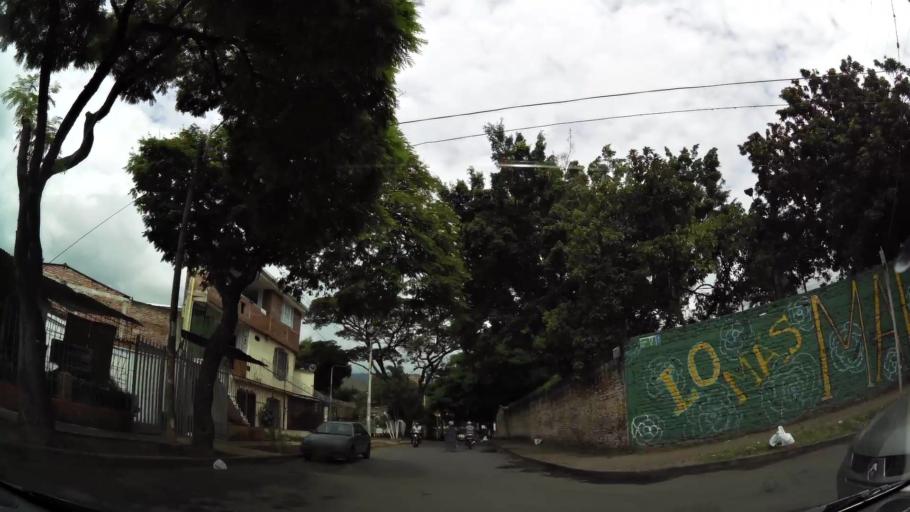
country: CO
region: Valle del Cauca
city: Cali
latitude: 3.3912
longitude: -76.5517
